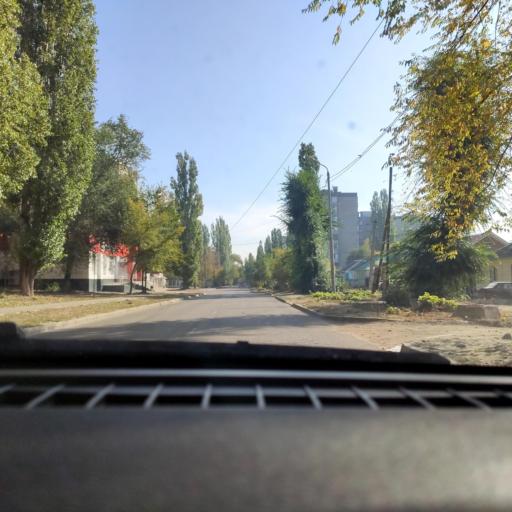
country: RU
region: Voronezj
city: Maslovka
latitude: 51.6335
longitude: 39.2804
